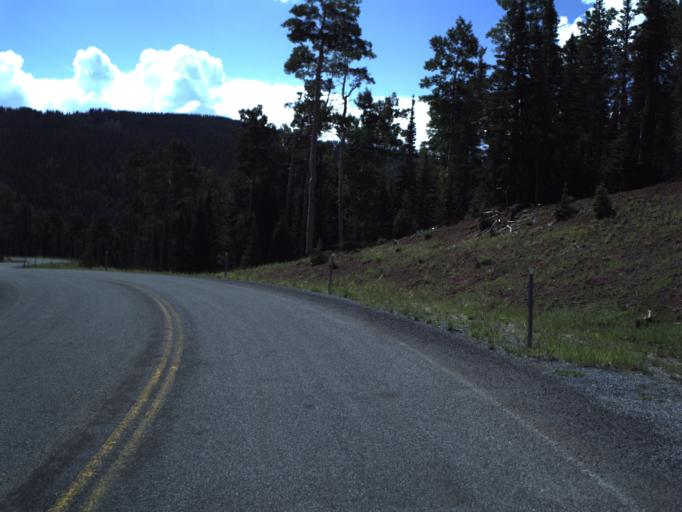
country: US
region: Utah
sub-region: Piute County
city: Junction
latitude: 38.3207
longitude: -112.3724
